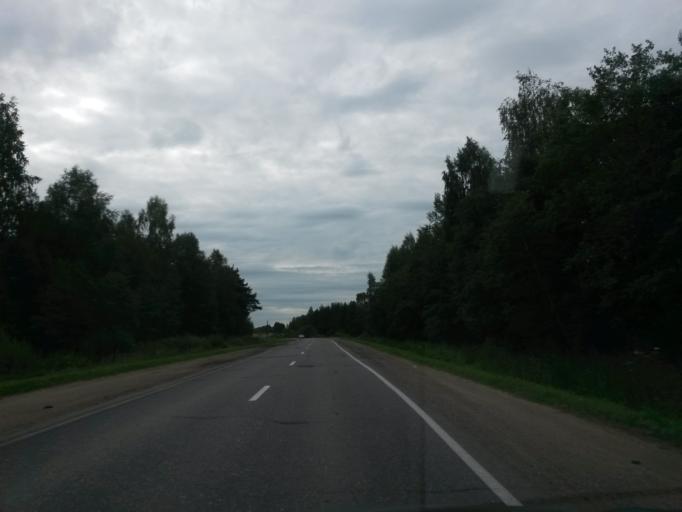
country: RU
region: Jaroslavl
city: Krasnyye Tkachi
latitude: 57.4000
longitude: 39.6655
